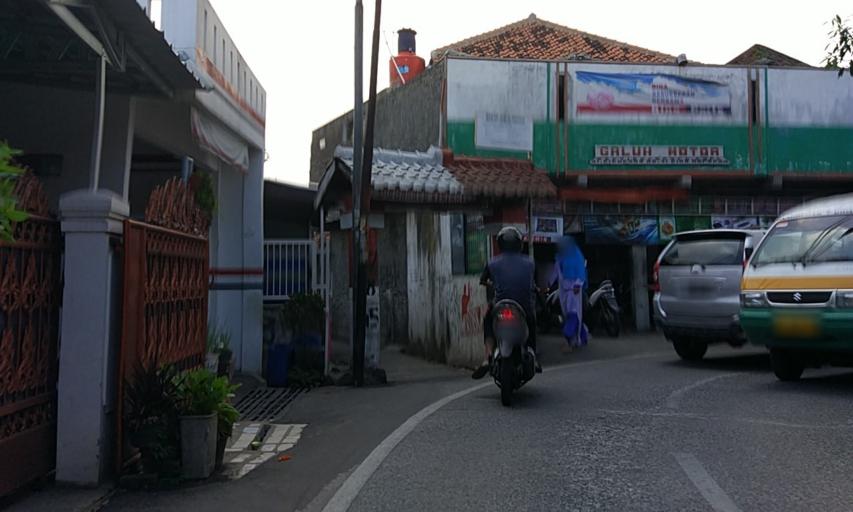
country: ID
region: West Java
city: Bandung
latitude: -6.9142
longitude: 107.6841
